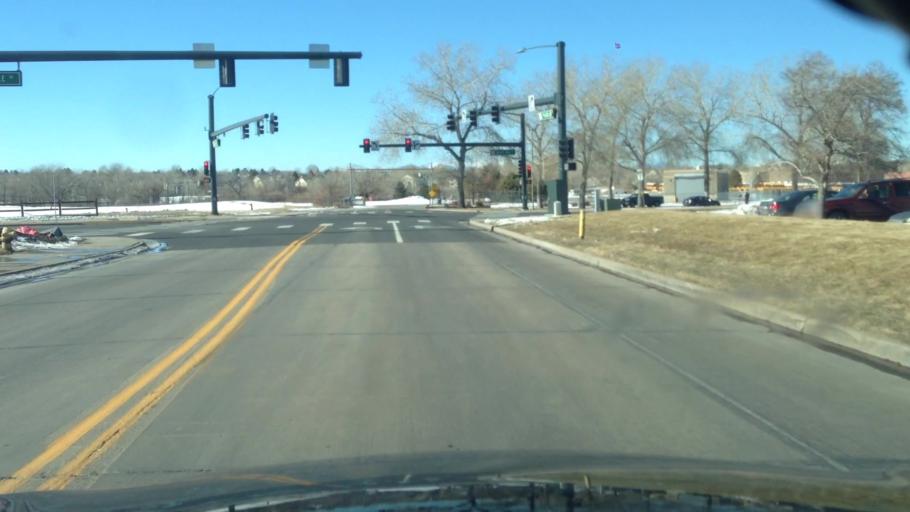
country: US
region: Colorado
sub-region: Douglas County
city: Parker
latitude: 39.5264
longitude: -104.7764
